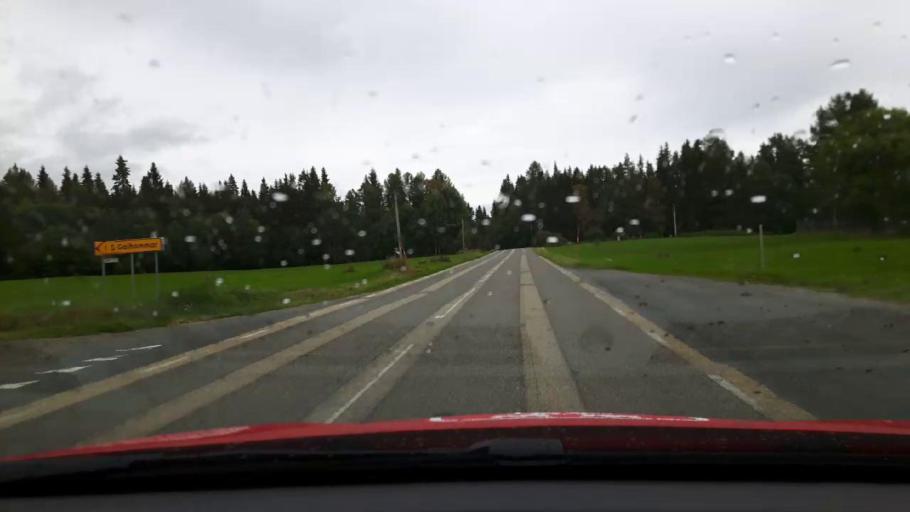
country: SE
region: Jaemtland
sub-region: Bergs Kommun
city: Hoverberg
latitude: 62.7821
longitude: 14.4338
